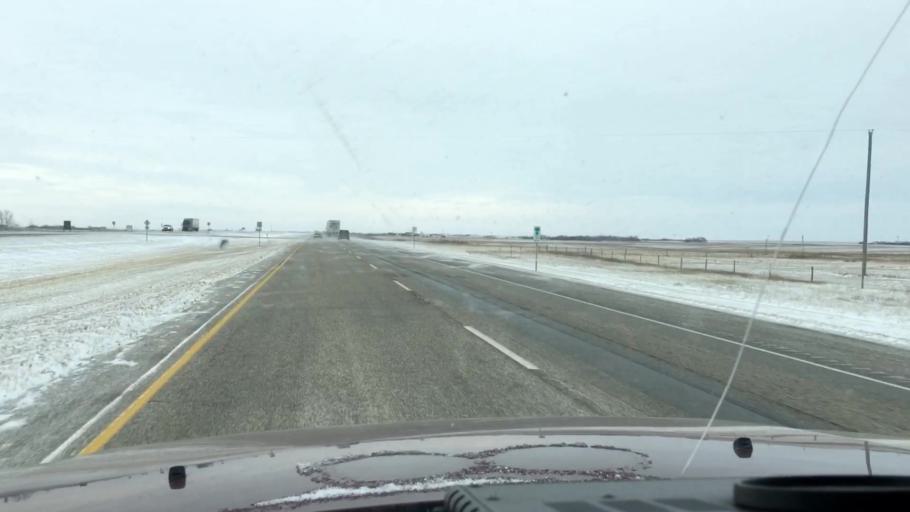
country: CA
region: Saskatchewan
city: Saskatoon
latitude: 51.6214
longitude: -106.4194
